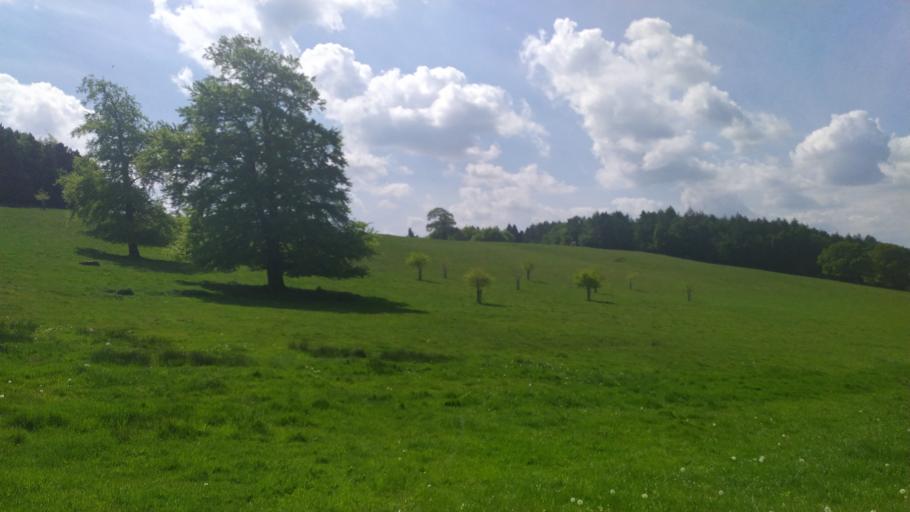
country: GB
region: England
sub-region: City and Borough of Leeds
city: Shadwell
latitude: 53.8845
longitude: -1.5185
